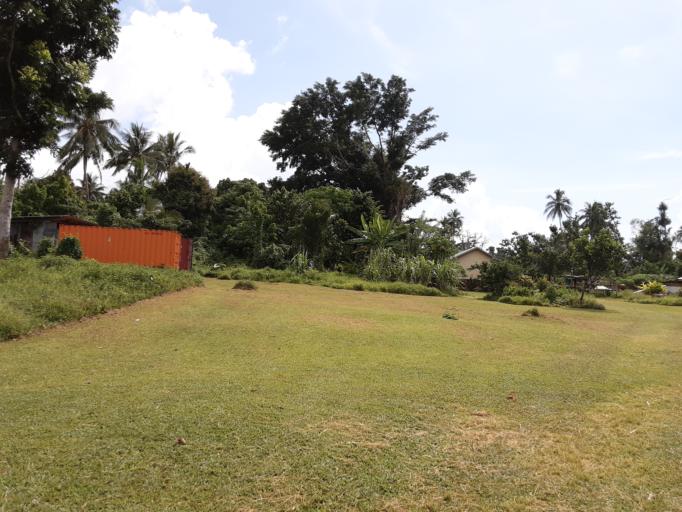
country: VU
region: Sanma
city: Luganville
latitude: -15.5799
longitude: 167.0009
